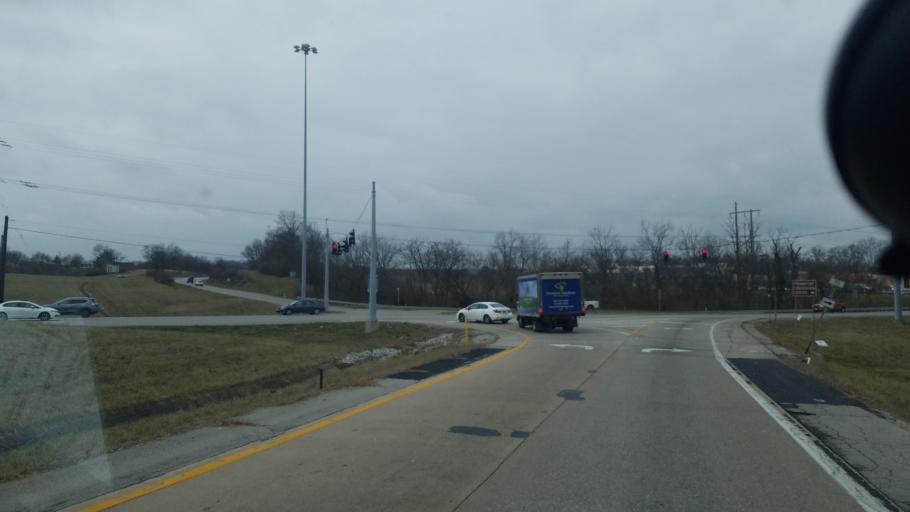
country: US
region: Kentucky
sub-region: Franklin County
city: Frankfort
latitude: 38.1747
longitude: -84.8111
